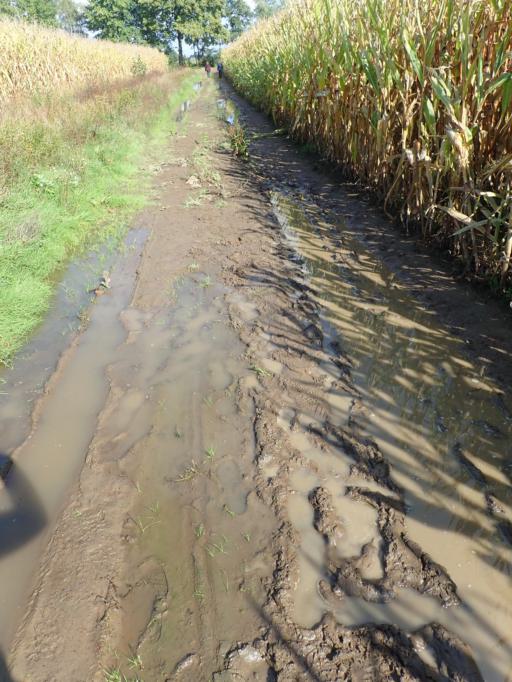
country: BE
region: Flanders
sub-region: Provincie Antwerpen
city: Hulshout
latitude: 51.0882
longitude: 4.8069
